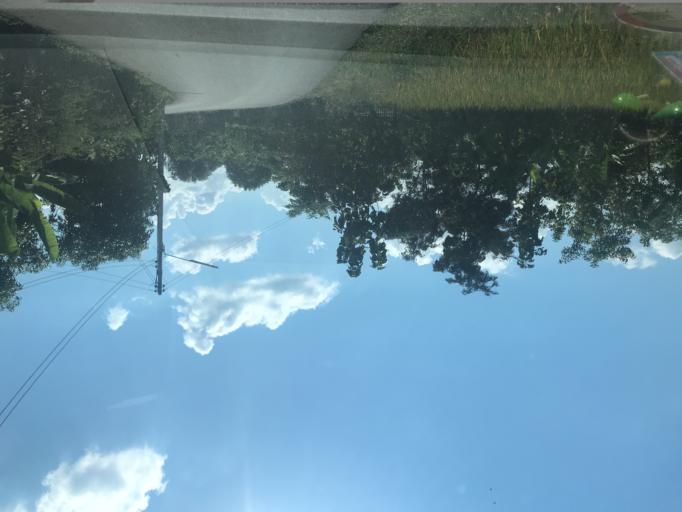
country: TH
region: Chiang Mai
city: Mae Wang
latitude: 18.5660
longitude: 98.8310
